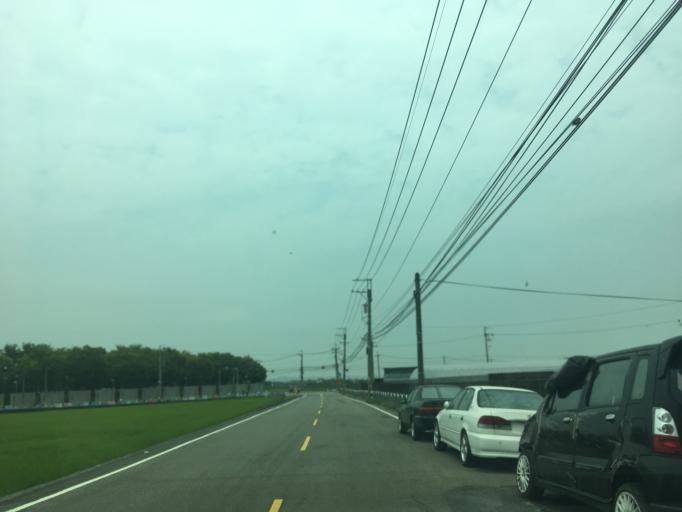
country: TW
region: Taiwan
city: Zhongxing New Village
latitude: 24.0274
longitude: 120.6901
